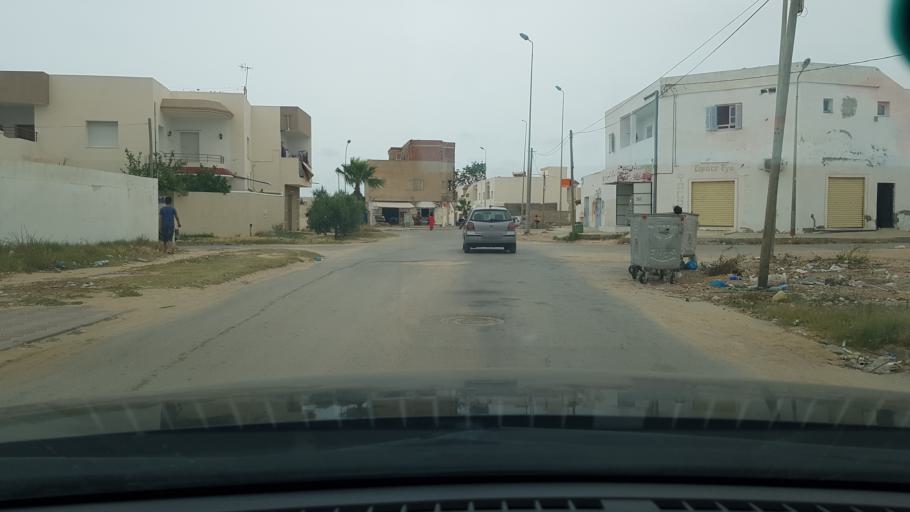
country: TN
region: Safaqis
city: Al Qarmadah
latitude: 34.8261
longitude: 10.7529
